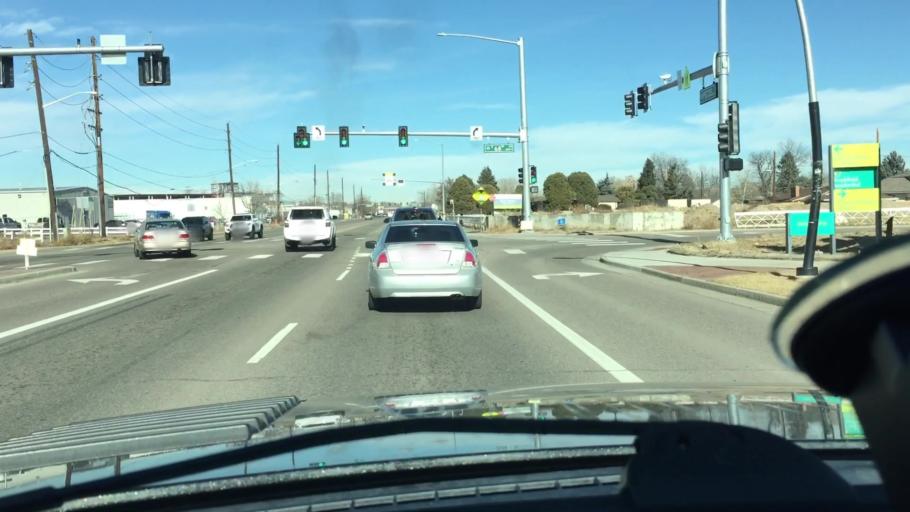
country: US
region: Colorado
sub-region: Adams County
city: Twin Lakes
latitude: 39.8197
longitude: -105.0062
